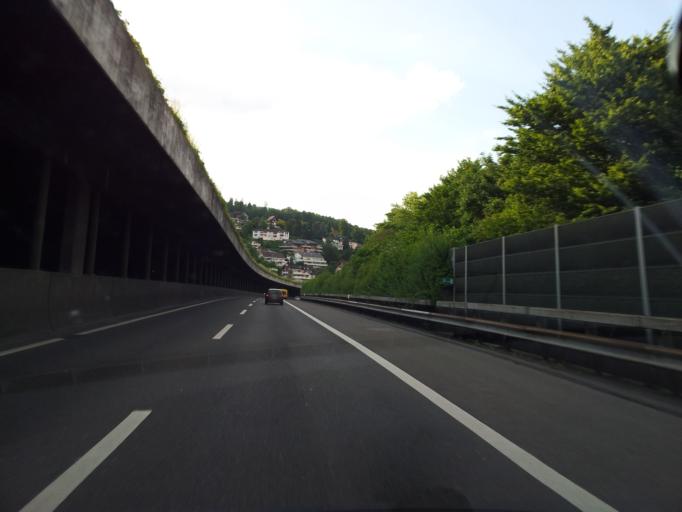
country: CH
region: Nidwalden
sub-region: Nidwalden
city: Hergiswil
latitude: 46.9903
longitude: 8.3084
